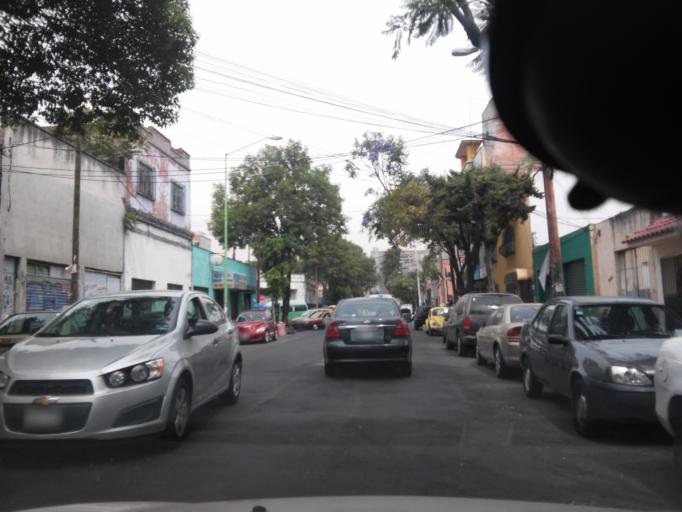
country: MX
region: Mexico City
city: Cuauhtemoc
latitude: 19.4432
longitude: -99.1673
